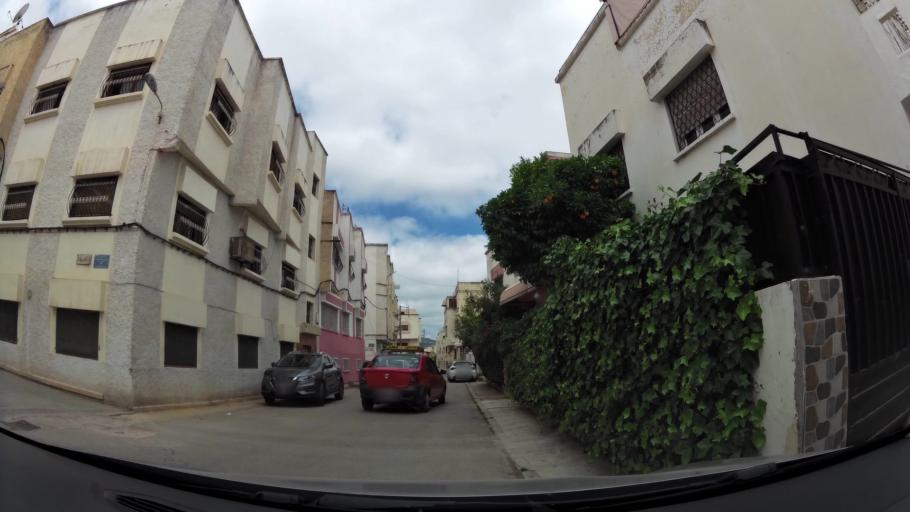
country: MA
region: Fes-Boulemane
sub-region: Fes
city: Fes
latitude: 34.0367
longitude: -5.0174
